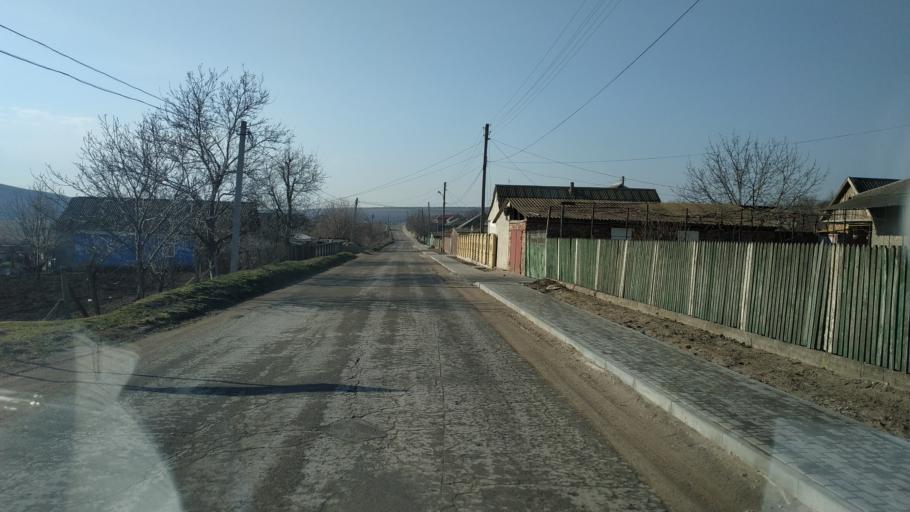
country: MD
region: Chisinau
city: Singera
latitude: 46.8093
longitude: 29.0359
